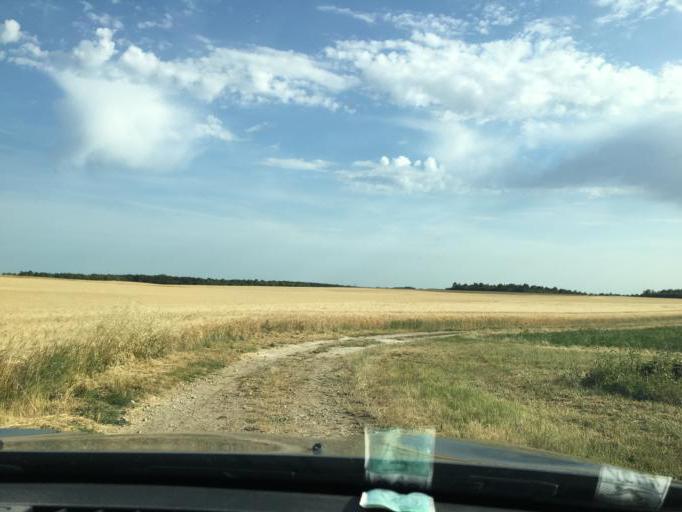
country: FR
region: Centre
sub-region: Departement du Loiret
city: Epieds-en-Beauce
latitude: 47.9339
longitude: 1.6111
